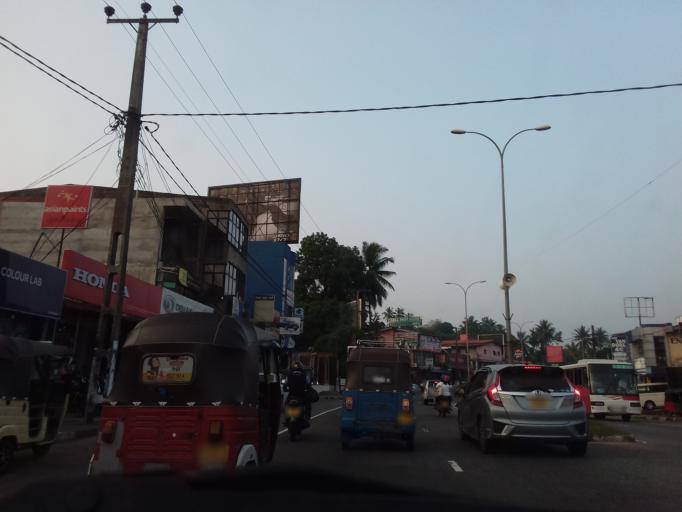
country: LK
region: Western
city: Kelaniya
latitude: 6.9989
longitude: 79.9481
